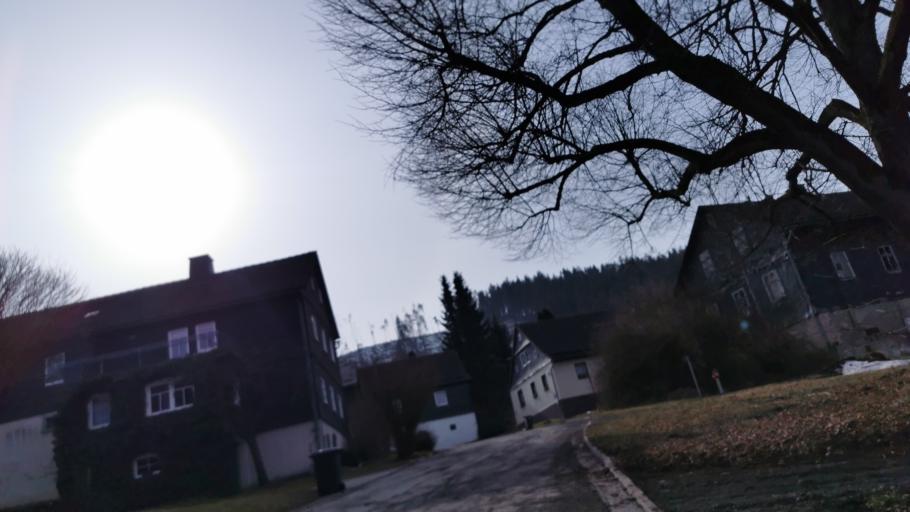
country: DE
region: Bavaria
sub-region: Upper Franconia
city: Ludwigsstadt
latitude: 50.4838
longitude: 11.4033
